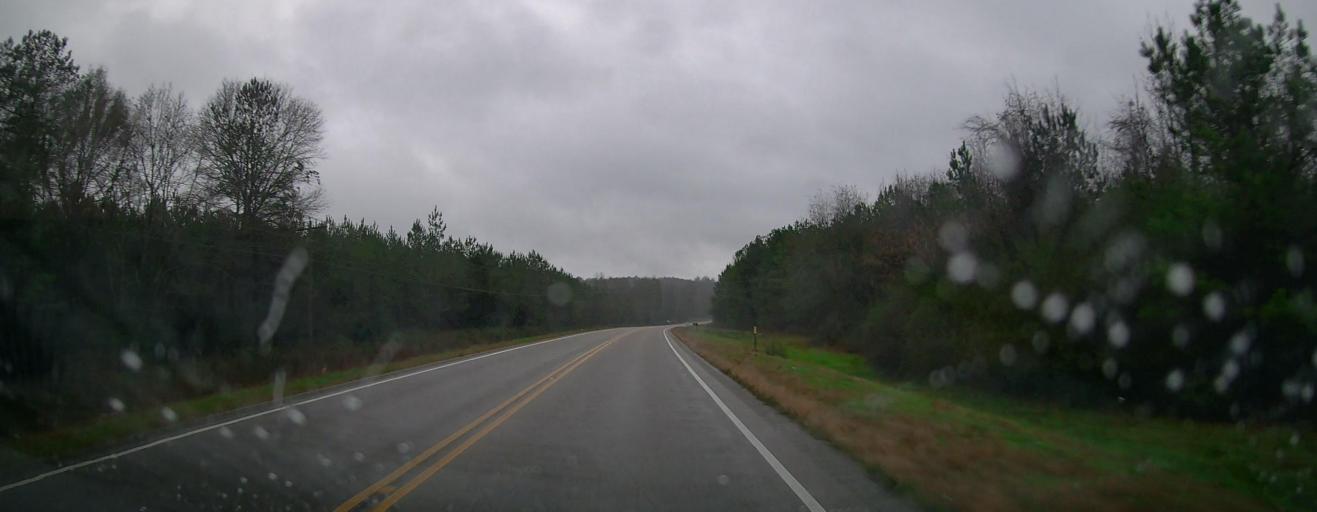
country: US
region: Alabama
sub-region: Autauga County
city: Prattville
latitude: 32.4936
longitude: -86.5767
